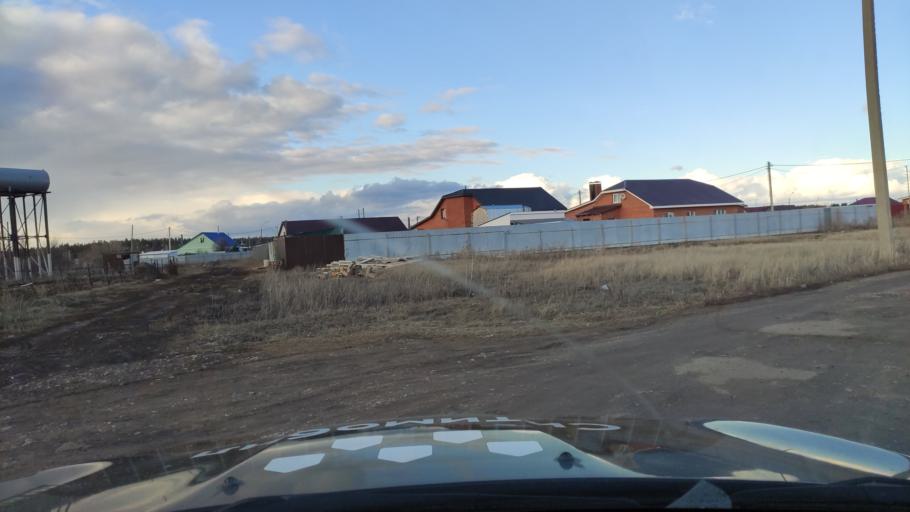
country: RU
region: Samara
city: Povolzhskiy
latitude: 53.5856
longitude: 49.7263
